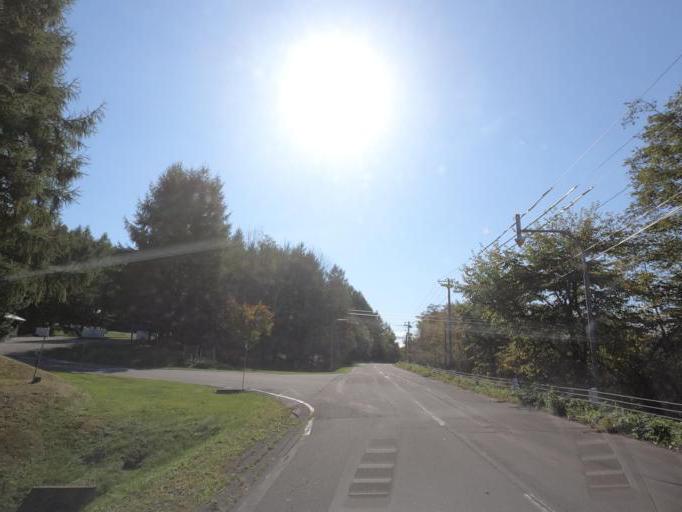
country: JP
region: Hokkaido
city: Obihiro
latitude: 42.6821
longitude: 143.4770
